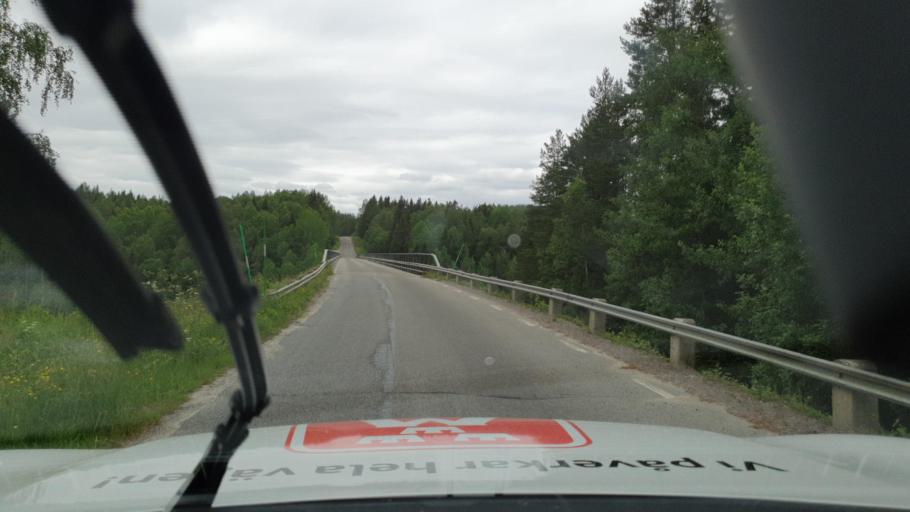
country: SE
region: Vaesterbotten
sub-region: Bjurholms Kommun
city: Bjurholm
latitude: 63.7953
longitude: 19.3504
